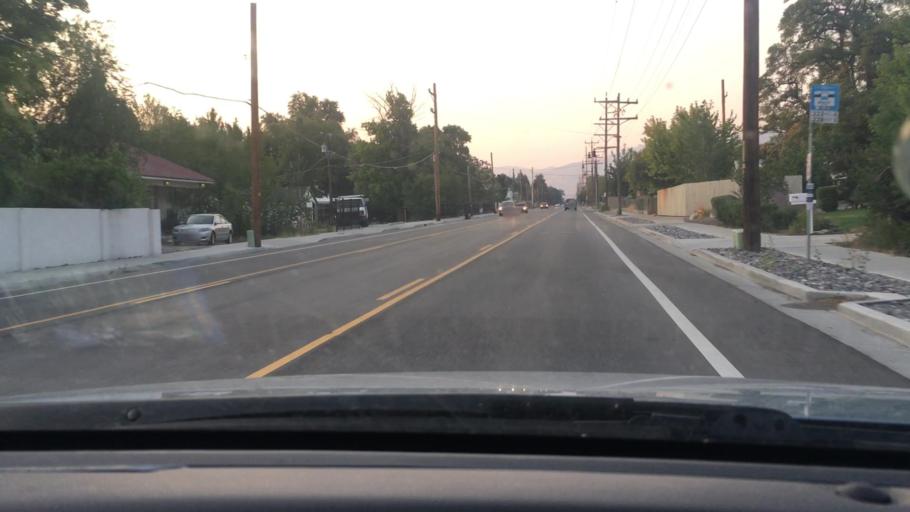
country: US
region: Utah
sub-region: Salt Lake County
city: East Millcreek
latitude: 40.6888
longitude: -111.8244
